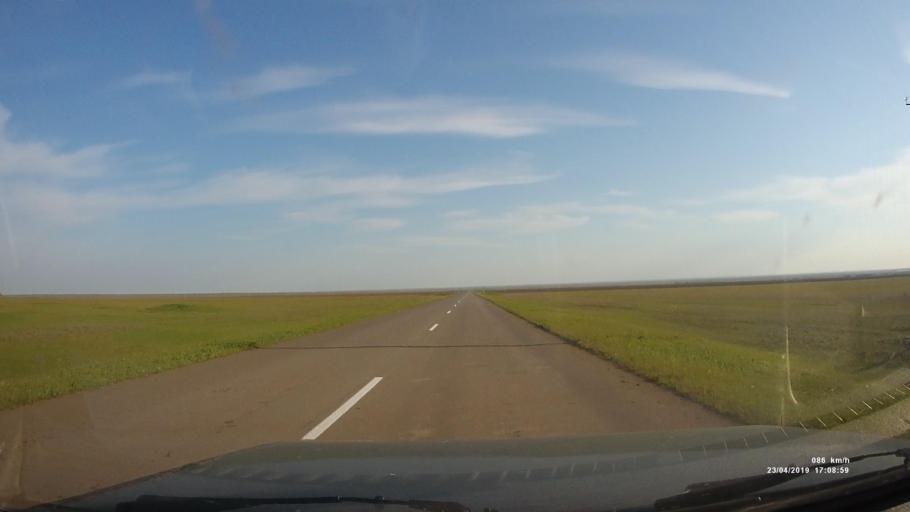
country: RU
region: Kalmykiya
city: Priyutnoye
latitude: 46.2647
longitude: 43.4843
